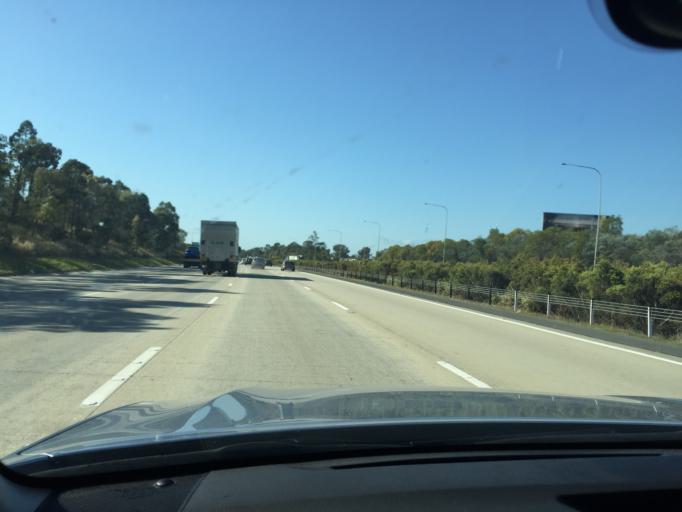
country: AU
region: Queensland
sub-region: Gold Coast
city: Yatala
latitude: -27.7533
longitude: 153.2375
